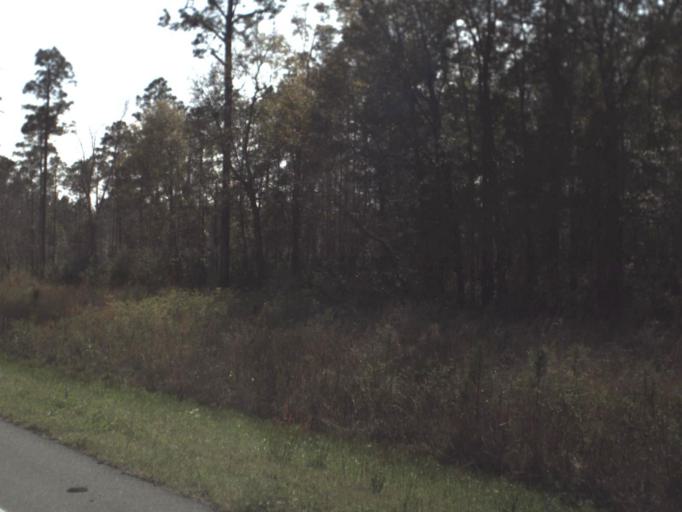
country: US
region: Florida
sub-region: Franklin County
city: Carrabelle
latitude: 29.9998
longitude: -84.5041
